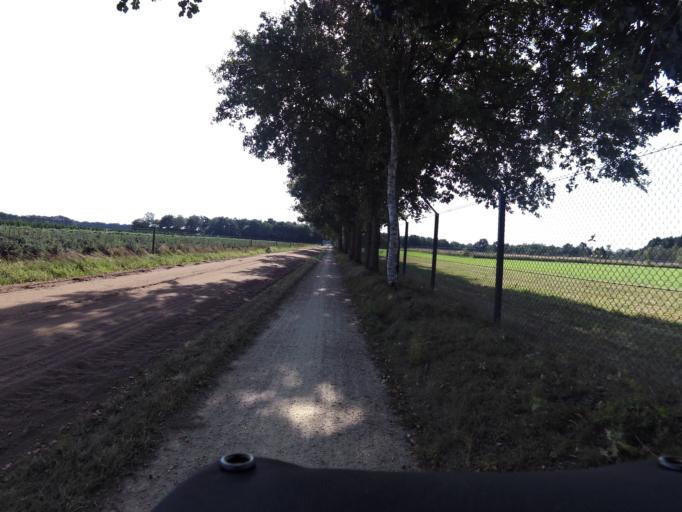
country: NL
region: Gelderland
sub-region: Gemeente Apeldoorn
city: Uddel
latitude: 52.2384
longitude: 5.7515
